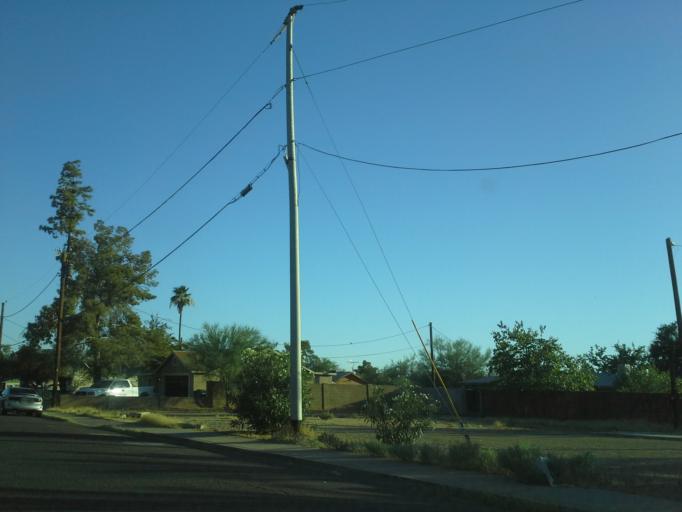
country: US
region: Arizona
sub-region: Maricopa County
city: Phoenix
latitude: 33.5677
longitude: -112.0588
